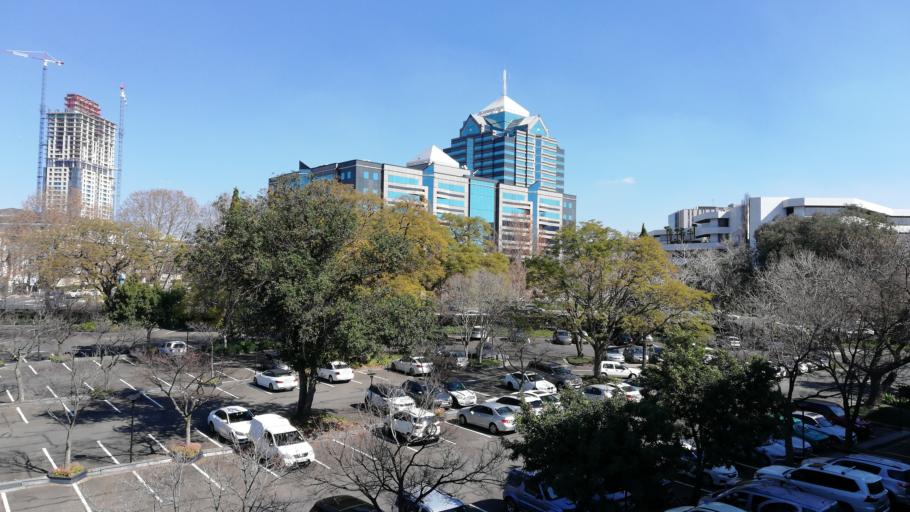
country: ZA
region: Gauteng
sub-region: City of Johannesburg Metropolitan Municipality
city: Johannesburg
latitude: -26.0994
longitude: 28.0595
